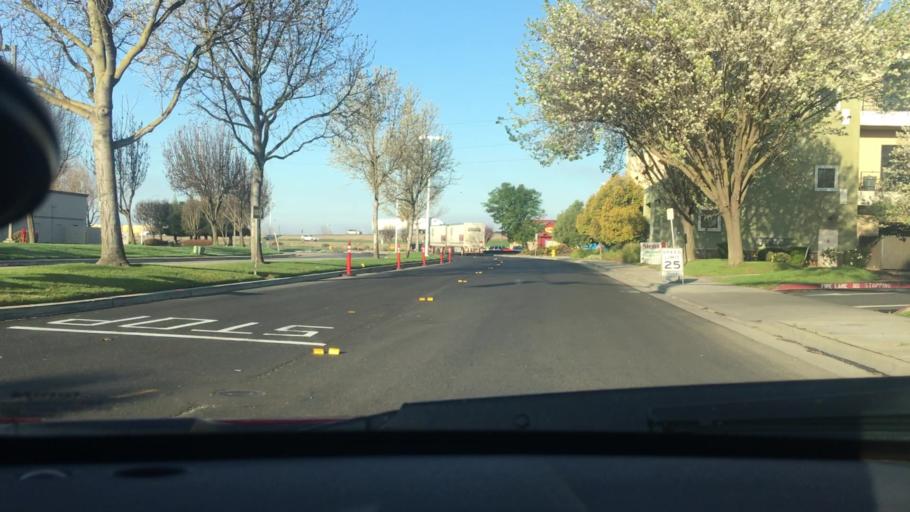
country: US
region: California
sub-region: San Joaquin County
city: Lathrop
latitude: 37.8101
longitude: -121.2935
